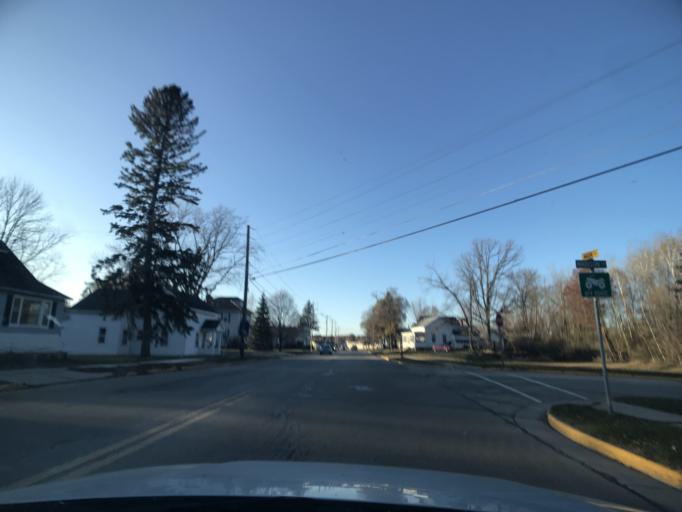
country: US
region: Wisconsin
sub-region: Oconto County
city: Oconto
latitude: 44.8916
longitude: -87.8798
